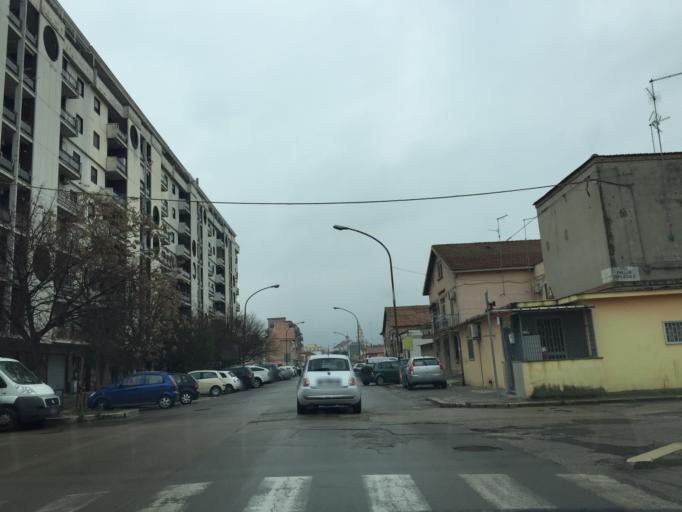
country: IT
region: Apulia
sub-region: Provincia di Foggia
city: Foggia
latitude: 41.4693
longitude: 15.5397
